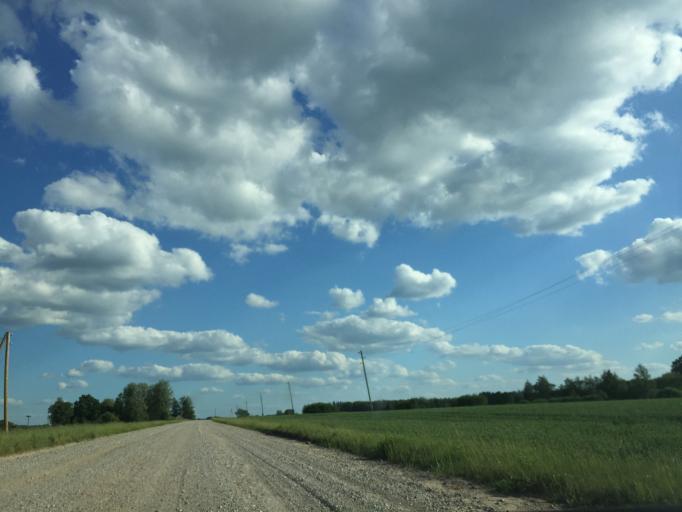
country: LV
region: Kandava
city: Kandava
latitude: 56.9131
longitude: 22.7915
